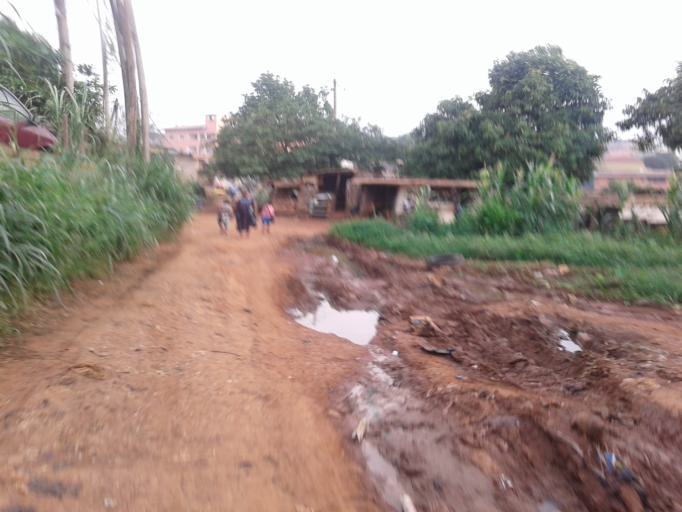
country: CM
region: Centre
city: Yaounde
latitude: 3.9087
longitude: 11.5291
